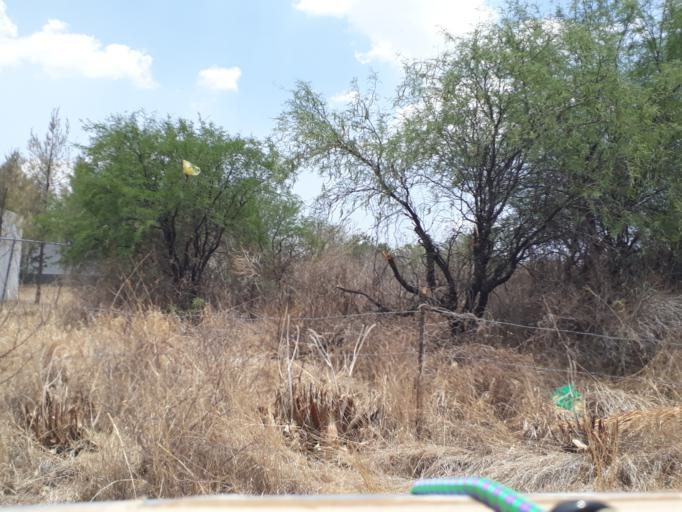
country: MX
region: Aguascalientes
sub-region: Aguascalientes
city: San Sebastian [Fraccionamiento]
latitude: 21.7777
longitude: -102.3278
